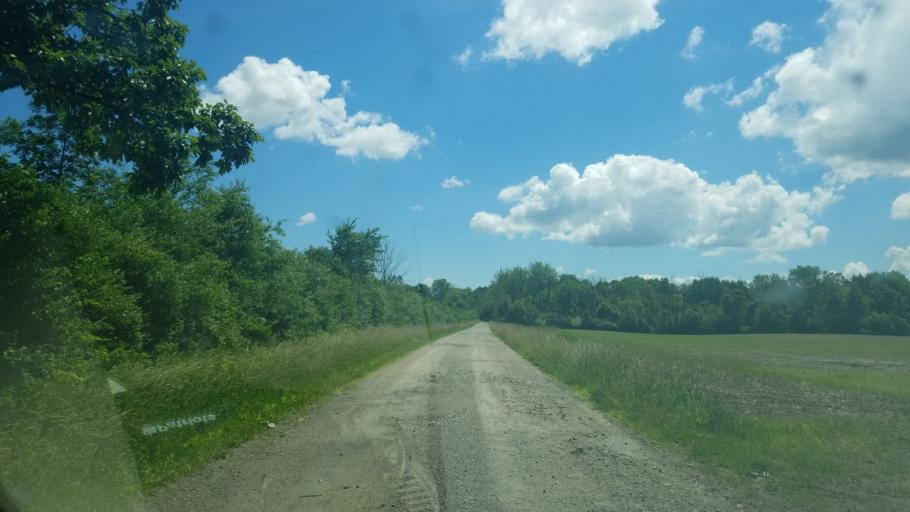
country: US
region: Ohio
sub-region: Huron County
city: New London
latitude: 41.1506
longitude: -82.3999
